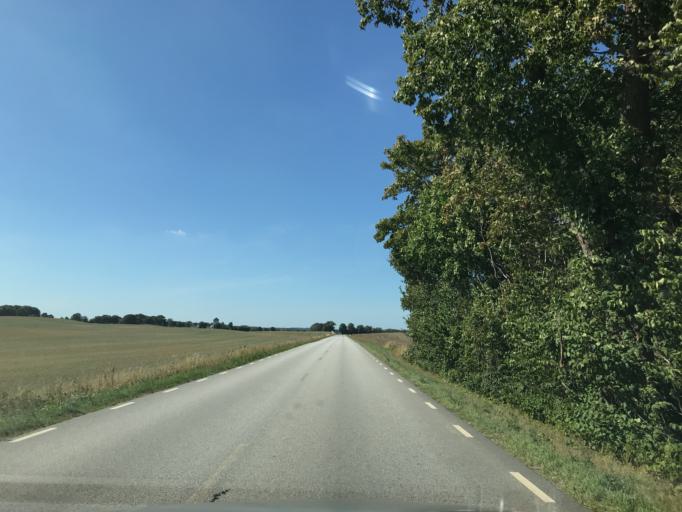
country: SE
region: Skane
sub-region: Tomelilla Kommun
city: Tomelilla
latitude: 55.6428
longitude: 13.9970
